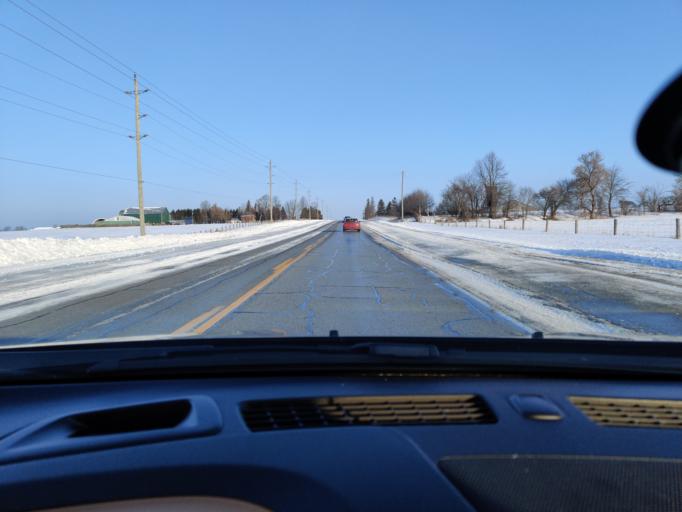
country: CA
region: Ontario
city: Angus
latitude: 44.3805
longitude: -79.7869
